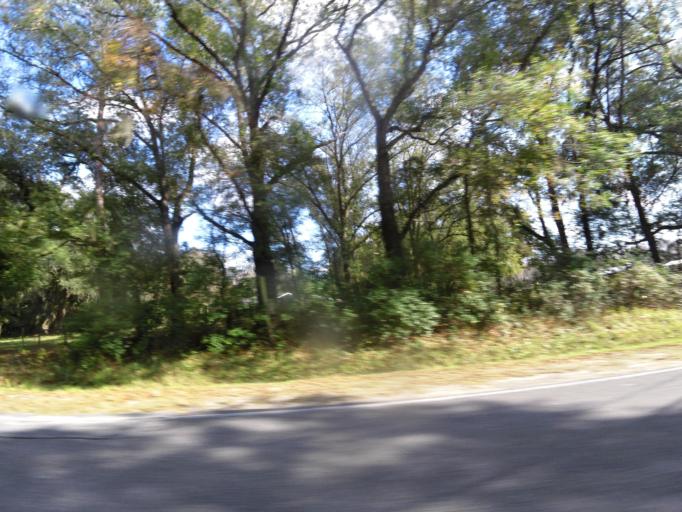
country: US
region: Florida
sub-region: Duval County
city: Baldwin
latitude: 30.1844
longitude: -81.9916
